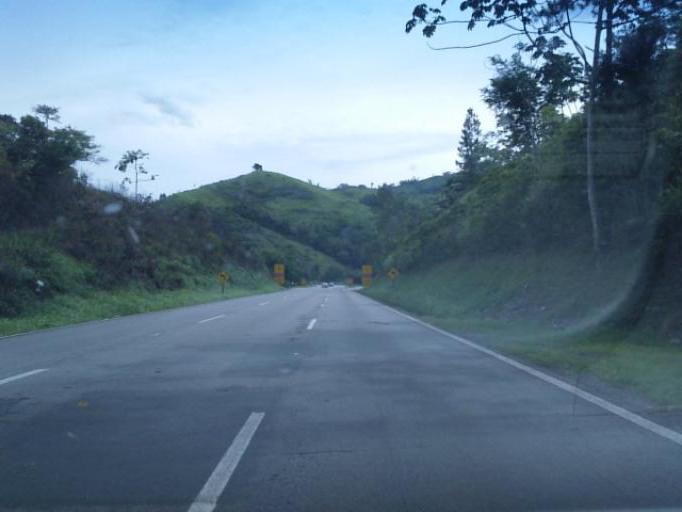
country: BR
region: Sao Paulo
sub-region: Cajati
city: Cajati
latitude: -24.7749
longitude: -48.2090
